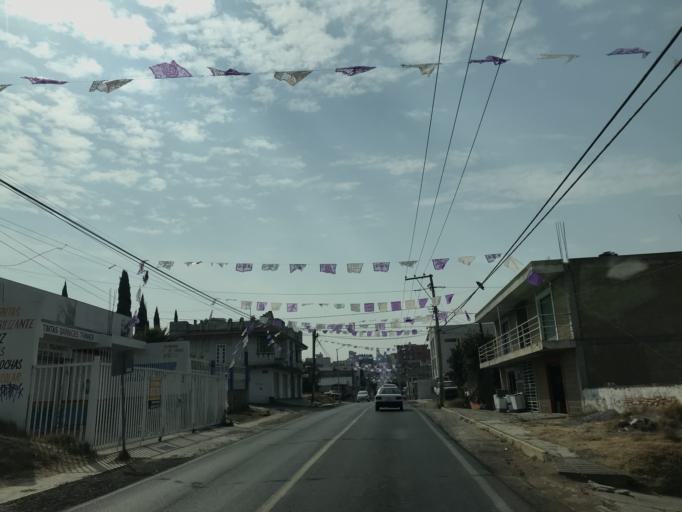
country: MX
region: Tlaxcala
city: Tenancingo
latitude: 19.1505
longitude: -98.2058
